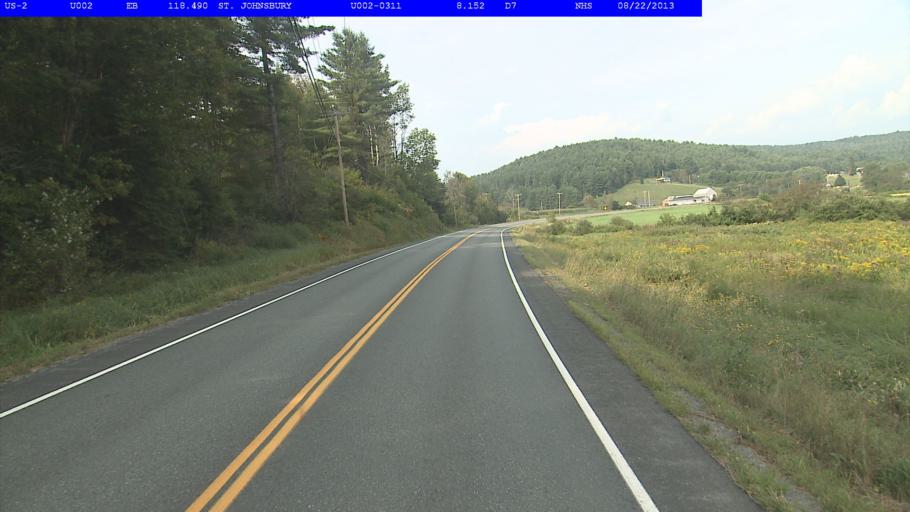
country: US
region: Vermont
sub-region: Caledonia County
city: St Johnsbury
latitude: 44.4455
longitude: -71.9445
